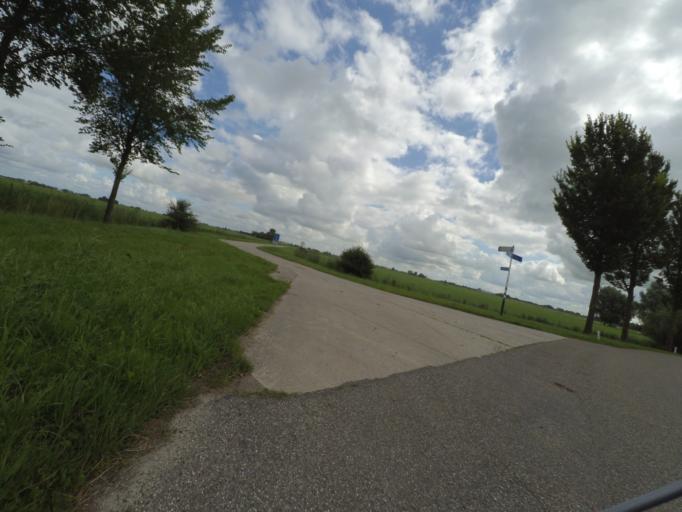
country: NL
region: Friesland
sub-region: Gemeente Kollumerland en Nieuwkruisland
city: Kollum
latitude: 53.2727
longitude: 6.1923
